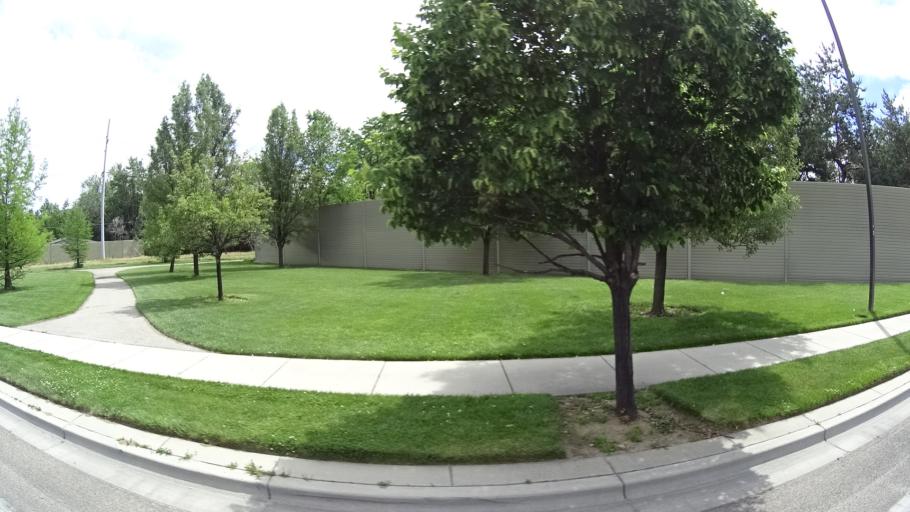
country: US
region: Idaho
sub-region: Ada County
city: Boise
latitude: 43.6047
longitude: -116.1873
